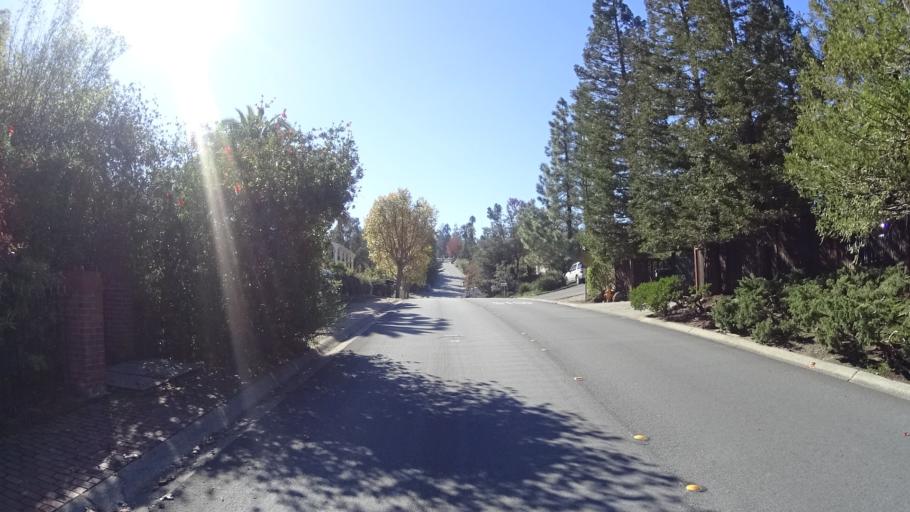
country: US
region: California
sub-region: San Mateo County
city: Hillsborough
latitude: 37.5680
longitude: -122.3730
